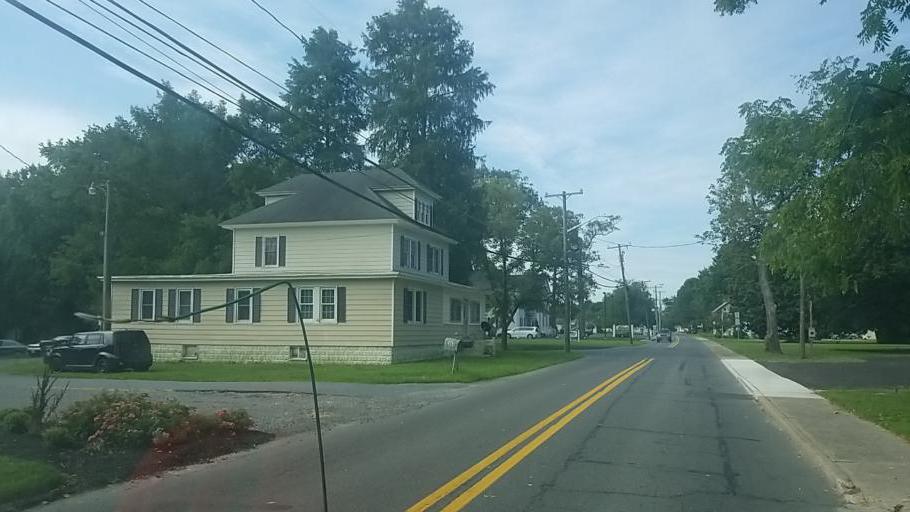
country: US
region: Delaware
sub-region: Sussex County
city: Selbyville
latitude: 38.5210
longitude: -75.2269
